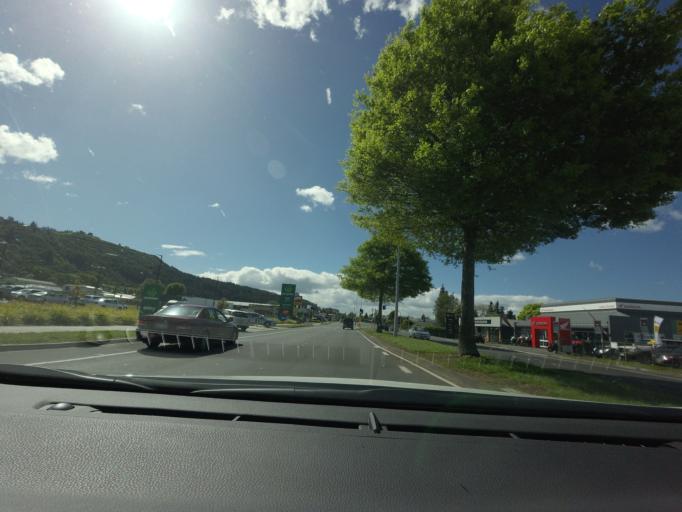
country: NZ
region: Bay of Plenty
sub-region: Rotorua District
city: Rotorua
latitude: -38.1202
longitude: 176.2287
